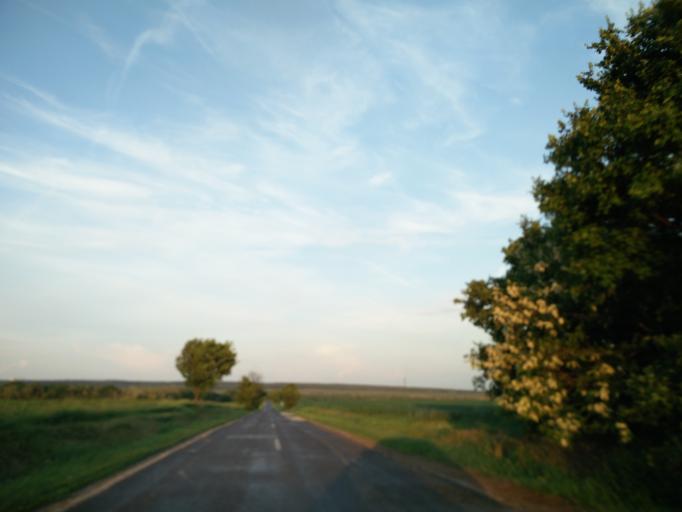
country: HU
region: Fejer
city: Bicske
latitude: 47.4321
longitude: 18.6594
